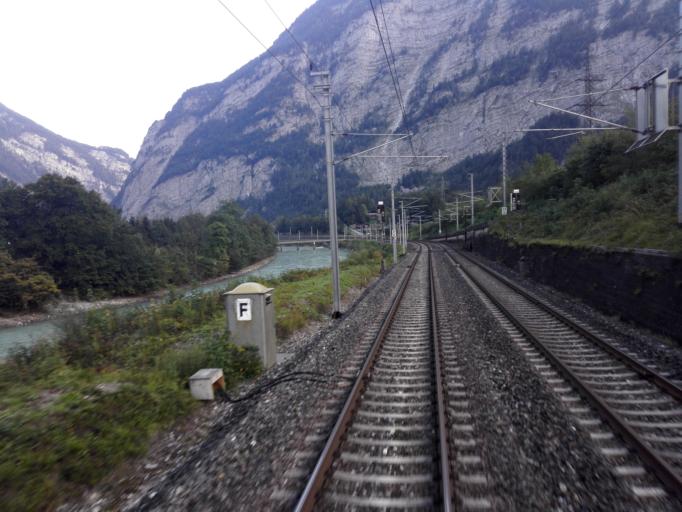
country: AT
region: Salzburg
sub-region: Politischer Bezirk Hallein
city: Golling an der Salzach
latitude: 47.5381
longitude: 13.1693
